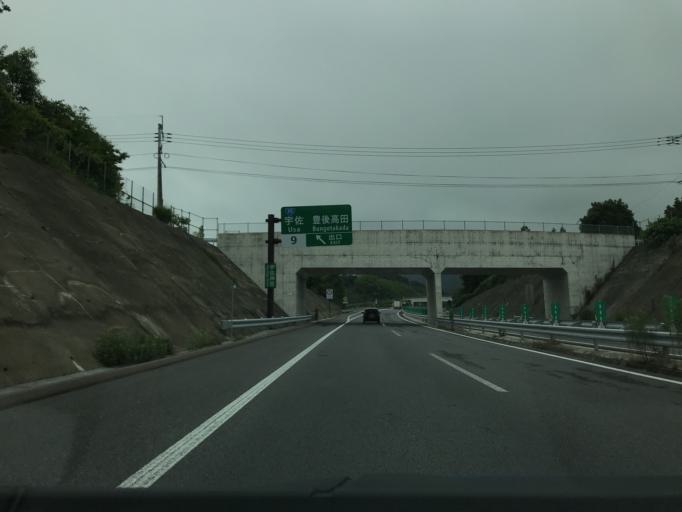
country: JP
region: Oita
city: Bungo-Takada-shi
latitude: 33.5009
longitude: 131.3151
